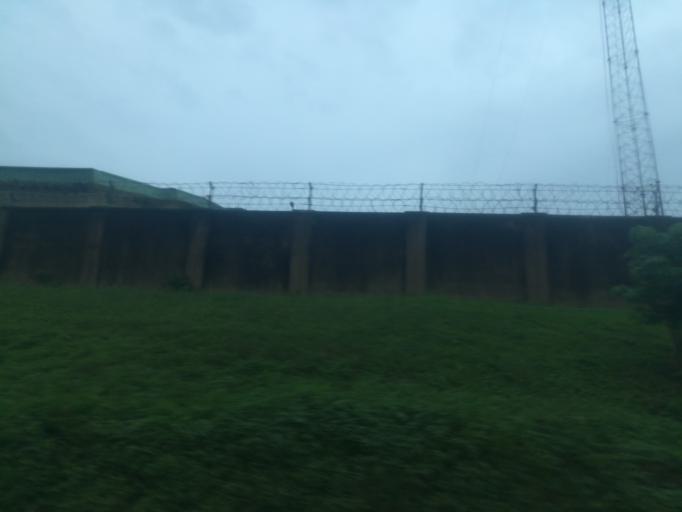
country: NG
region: Oyo
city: Ibadan
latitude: 7.4006
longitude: 3.9660
